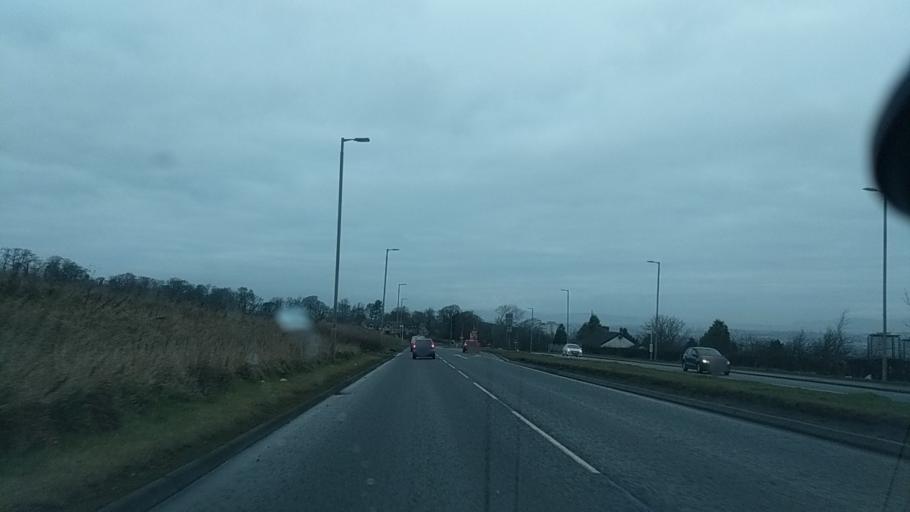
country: GB
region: Scotland
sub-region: South Lanarkshire
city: East Kilbride
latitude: 55.8010
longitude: -4.1773
